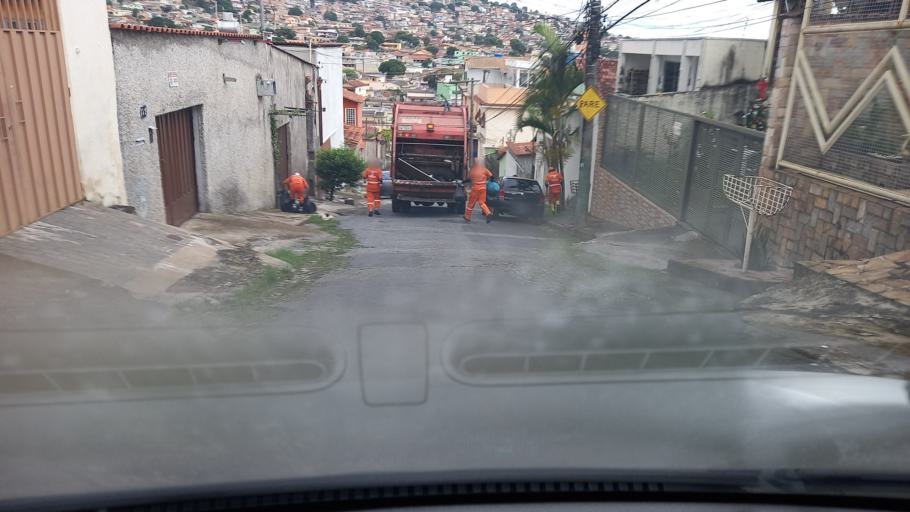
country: BR
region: Minas Gerais
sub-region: Contagem
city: Contagem
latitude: -19.9100
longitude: -44.0000
